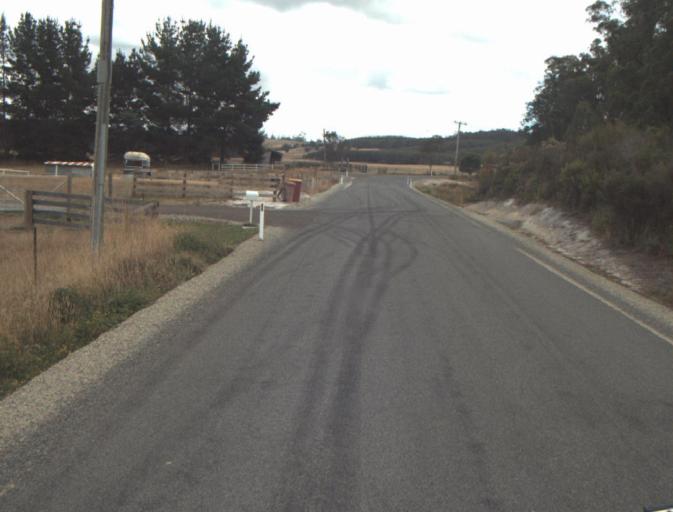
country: AU
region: Tasmania
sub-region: Launceston
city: Mayfield
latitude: -41.2094
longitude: 147.1881
